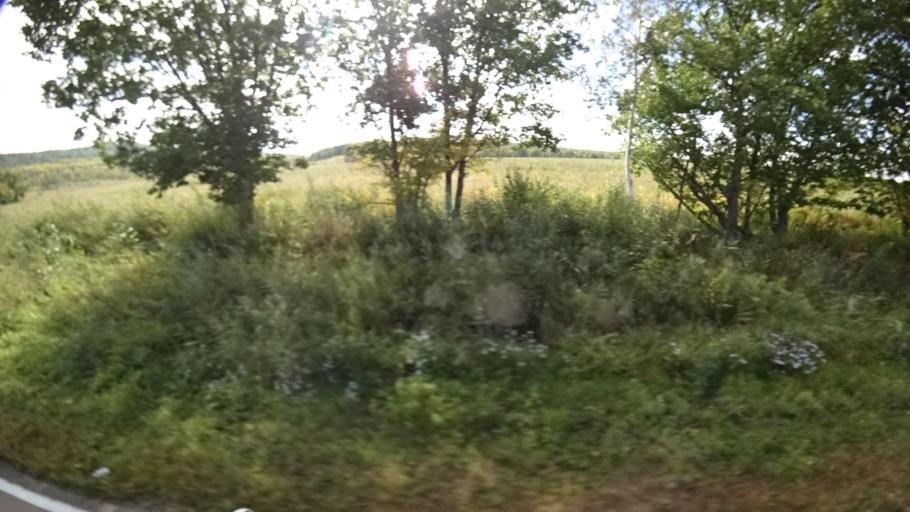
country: RU
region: Primorskiy
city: Yakovlevka
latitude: 44.4117
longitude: 133.5874
